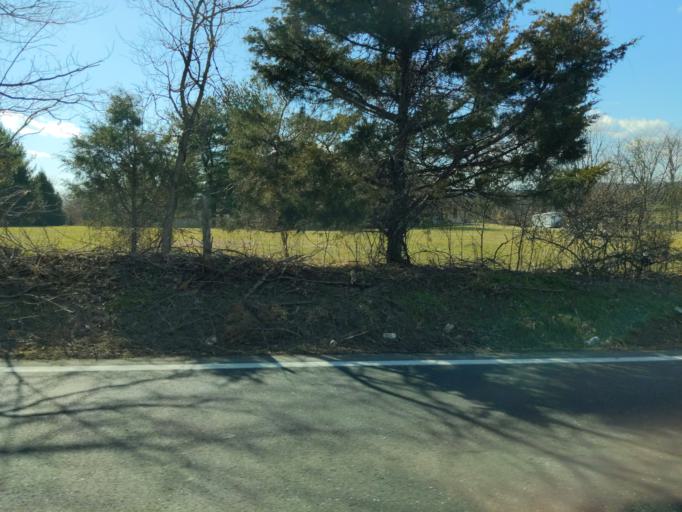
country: US
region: Pennsylvania
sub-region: Montgomery County
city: Pennsburg
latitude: 40.4083
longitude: -75.4730
